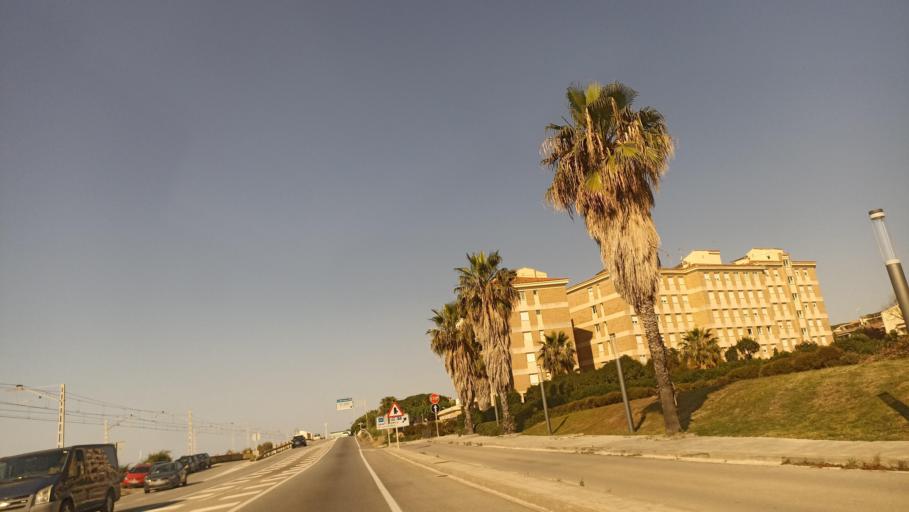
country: ES
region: Catalonia
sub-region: Provincia de Barcelona
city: Sant Andreu de Llavaneres
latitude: 41.5579
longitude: 2.5025
